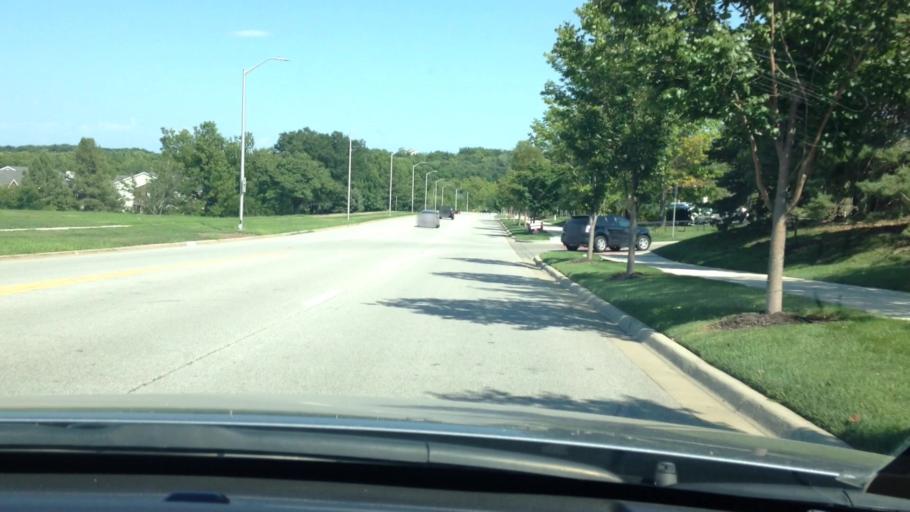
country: US
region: Kansas
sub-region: Johnson County
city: Leawood
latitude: 38.9165
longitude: -94.6385
